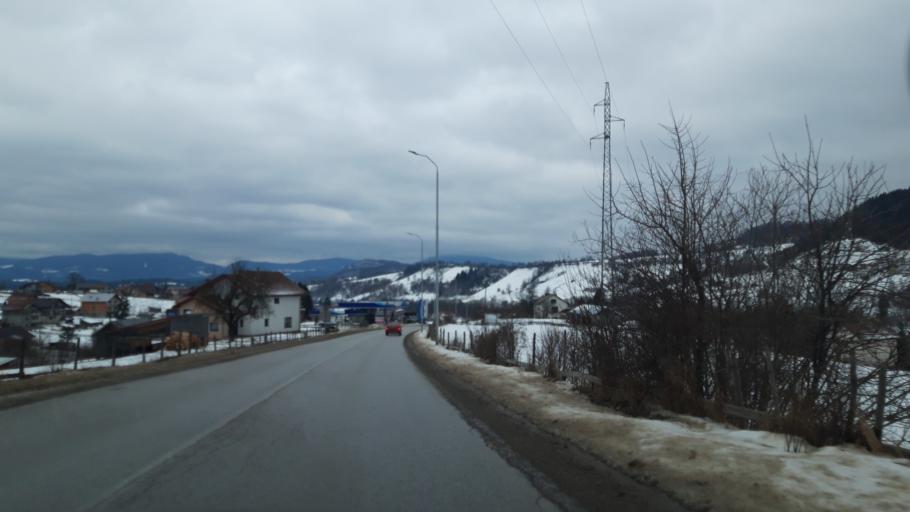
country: BA
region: Republika Srpska
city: Pale
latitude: 43.8882
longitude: 18.6156
